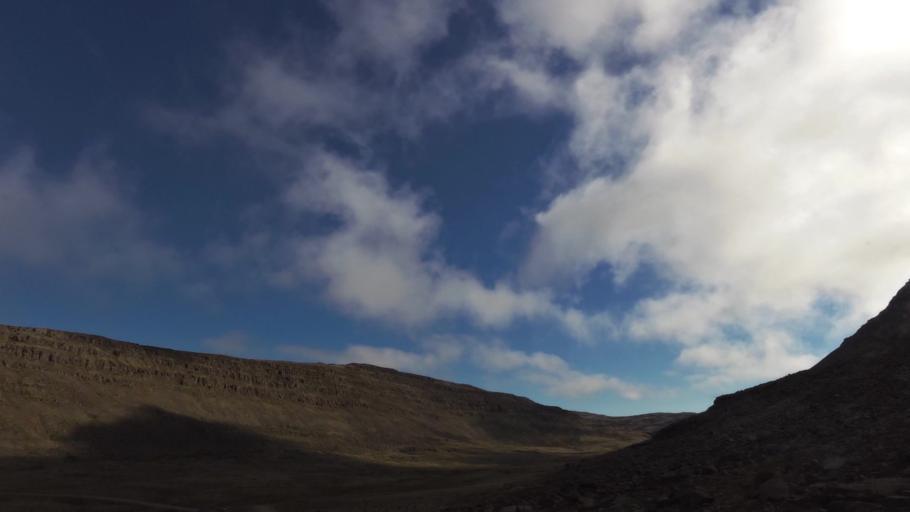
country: IS
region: West
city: Olafsvik
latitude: 65.5789
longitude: -24.0861
